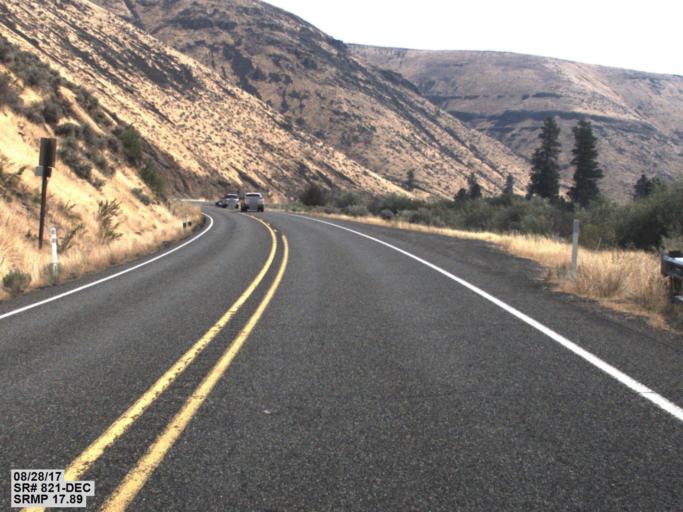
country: US
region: Washington
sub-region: Kittitas County
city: Kittitas
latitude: 46.8726
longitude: -120.4890
